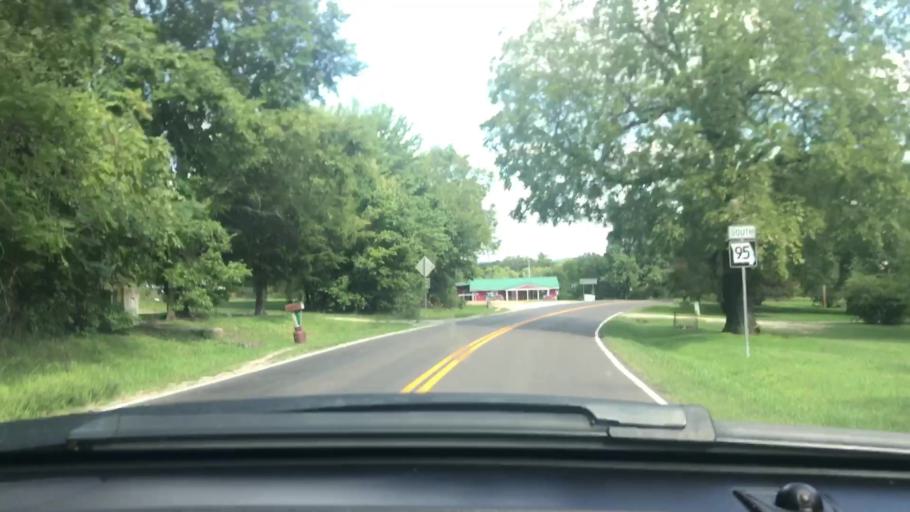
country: US
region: Missouri
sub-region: Wright County
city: Hartville
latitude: 37.3797
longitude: -92.3624
